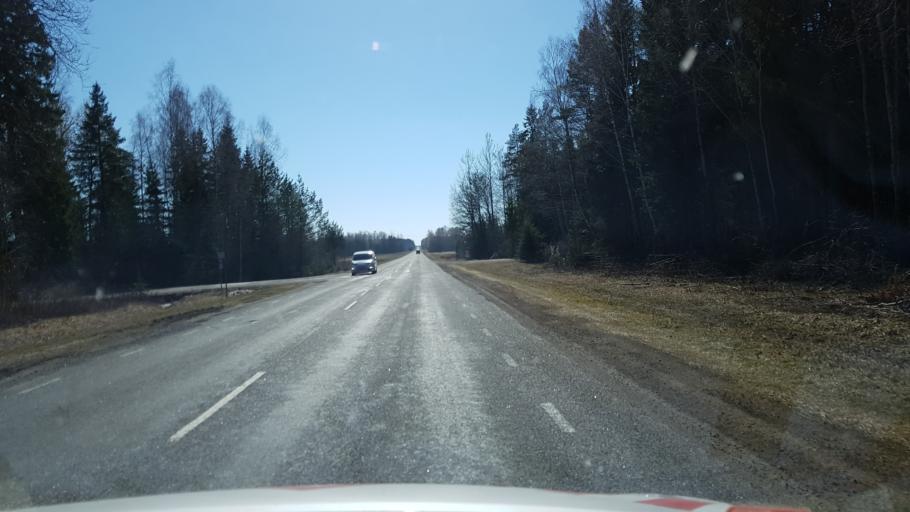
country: EE
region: Laeaene-Virumaa
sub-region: Tamsalu vald
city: Tamsalu
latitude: 59.1426
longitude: 26.0555
